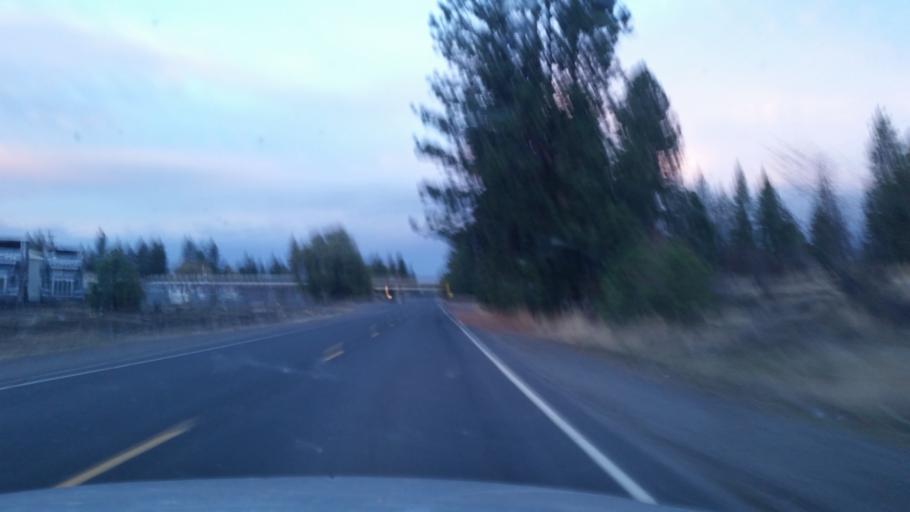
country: US
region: Washington
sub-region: Spokane County
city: Spokane
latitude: 47.6357
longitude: -117.4917
